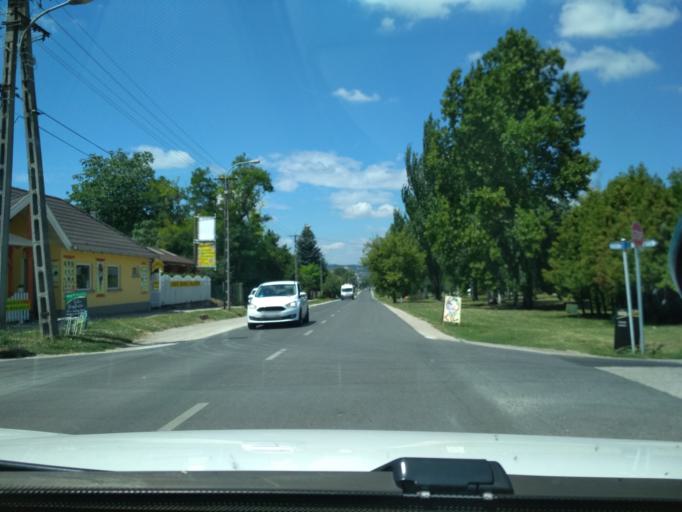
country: HU
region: Fejer
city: Kapolnasnyek
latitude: 47.2230
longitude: 18.6711
